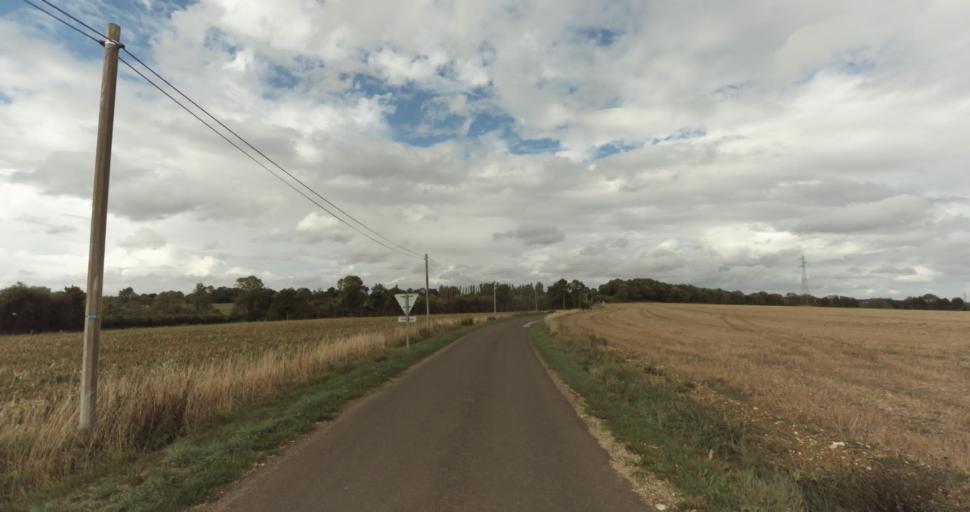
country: FR
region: Lower Normandy
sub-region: Departement de l'Orne
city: Sainte-Gauburge-Sainte-Colombe
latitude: 48.7460
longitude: 0.3746
